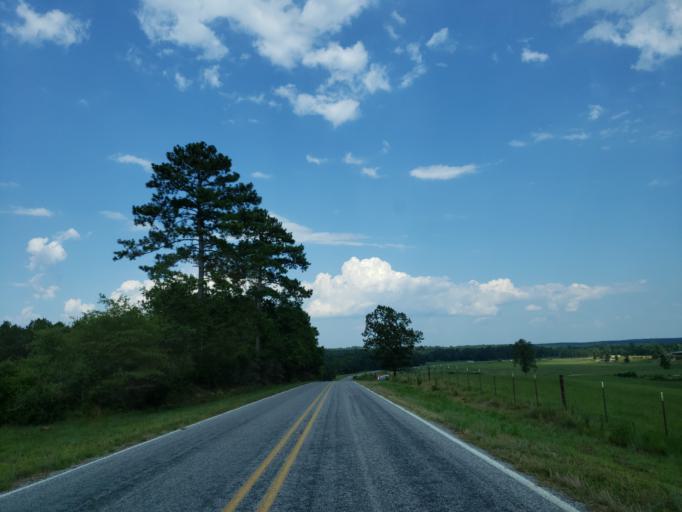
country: US
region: Mississippi
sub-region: Jones County
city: Ellisville
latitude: 31.6235
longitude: -89.3674
